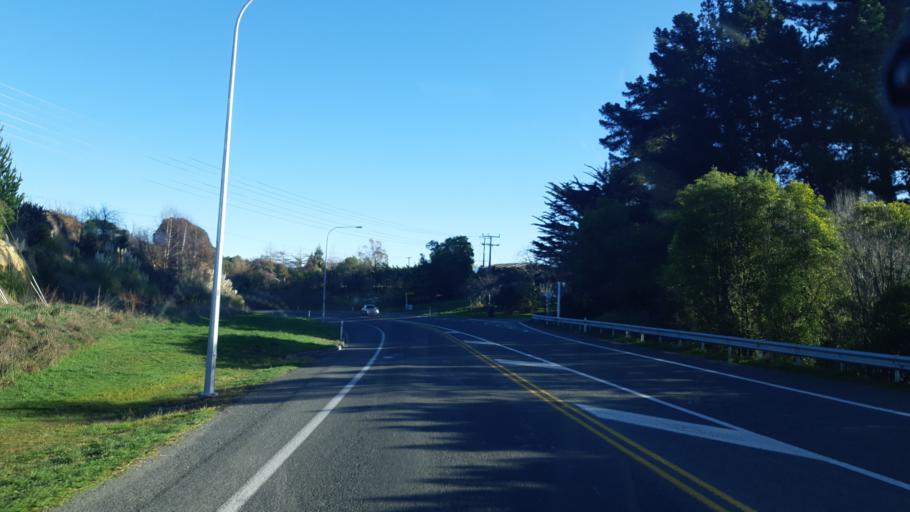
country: NZ
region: Tasman
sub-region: Tasman District
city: Mapua
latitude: -41.2955
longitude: 173.0983
